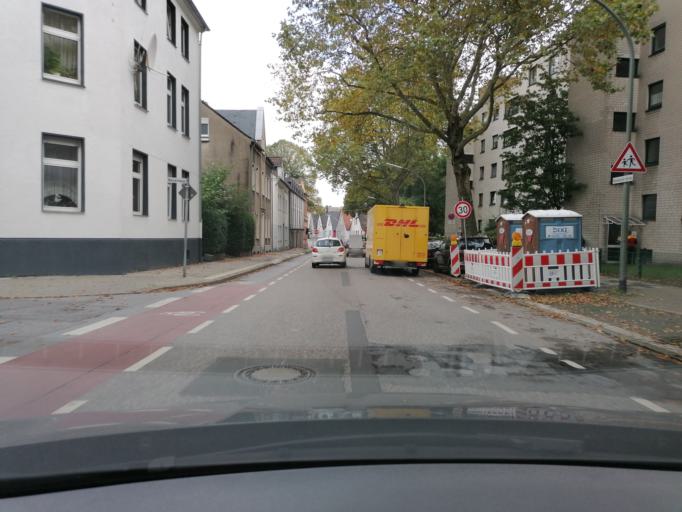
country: DE
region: North Rhine-Westphalia
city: Herten
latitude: 51.5799
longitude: 7.1109
